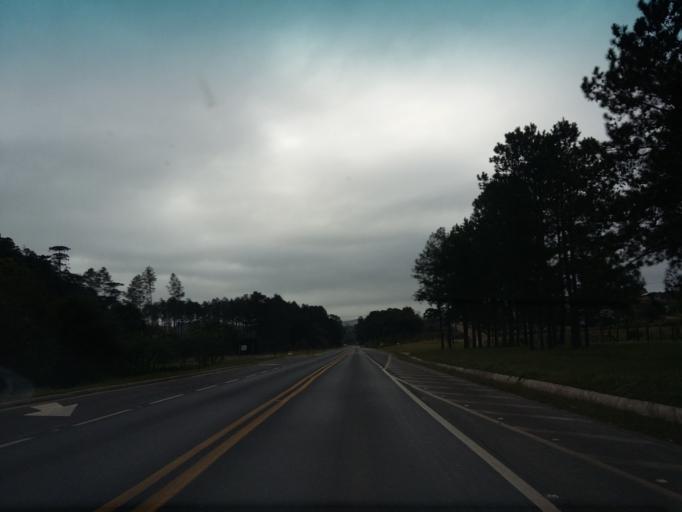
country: BR
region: Santa Catarina
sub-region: Santa Cecilia
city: Santa Cecilia
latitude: -26.7152
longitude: -50.3001
